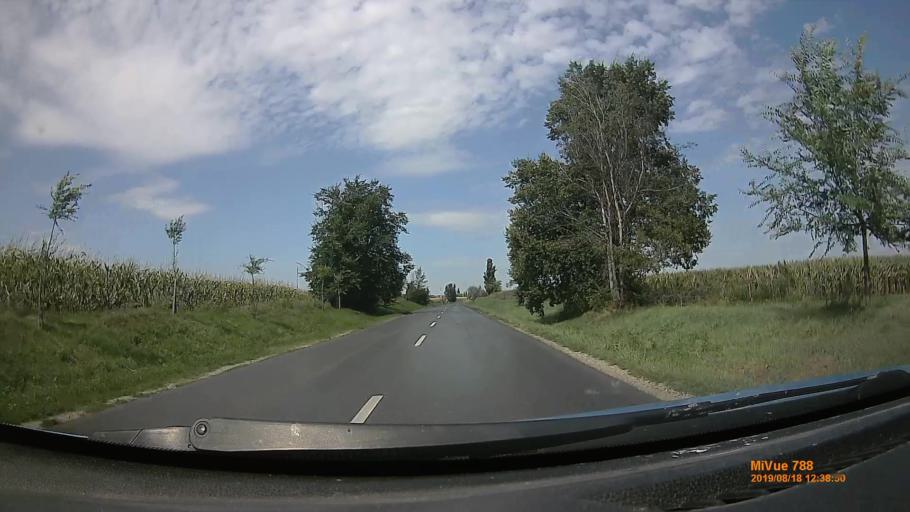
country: HU
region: Fejer
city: Szabadbattyan
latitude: 47.0923
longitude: 18.3952
